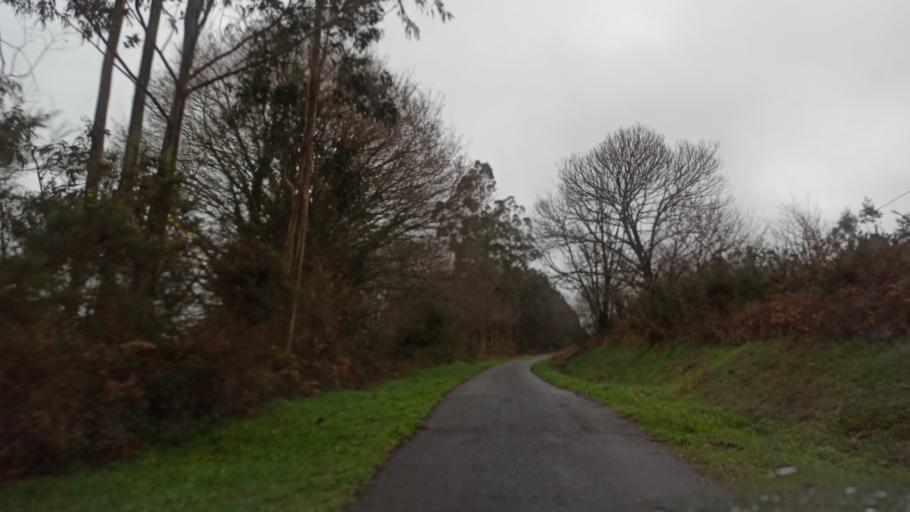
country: ES
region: Galicia
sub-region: Provincia da Coruna
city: Cesuras
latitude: 43.1794
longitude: -8.1551
